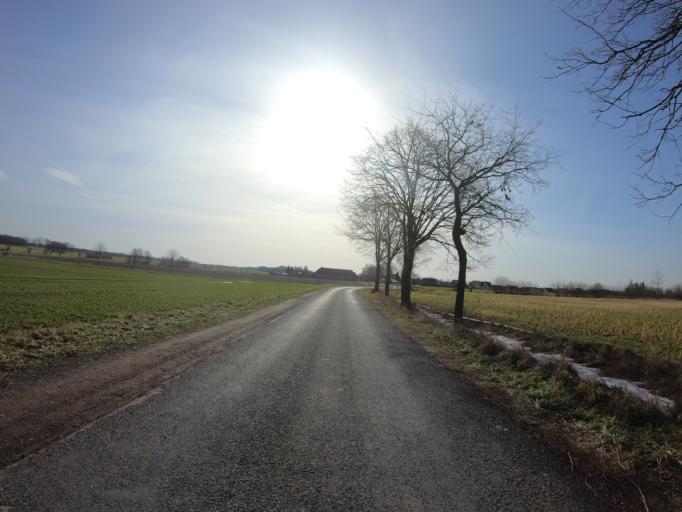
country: DE
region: Lower Saxony
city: Isenbuttel
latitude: 52.4132
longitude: 10.5646
